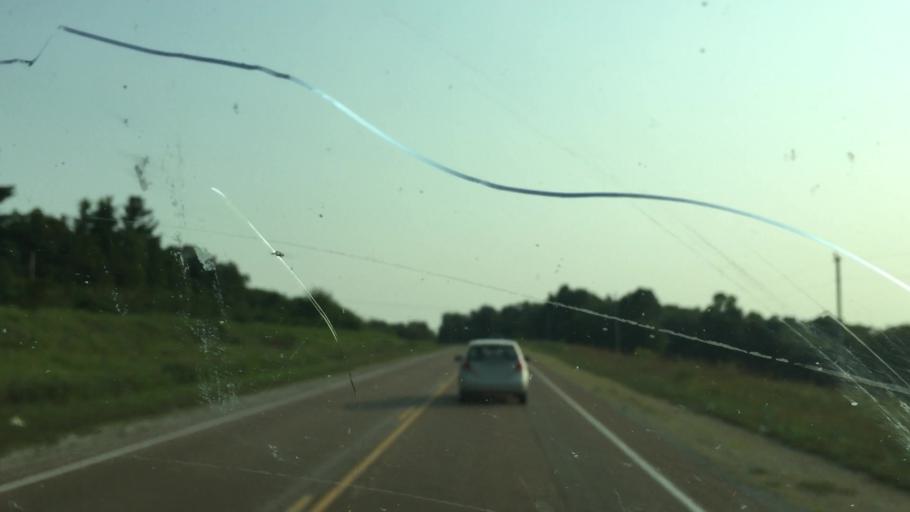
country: US
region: Missouri
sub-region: Pulaski County
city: Richland
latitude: 37.7883
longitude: -92.4094
